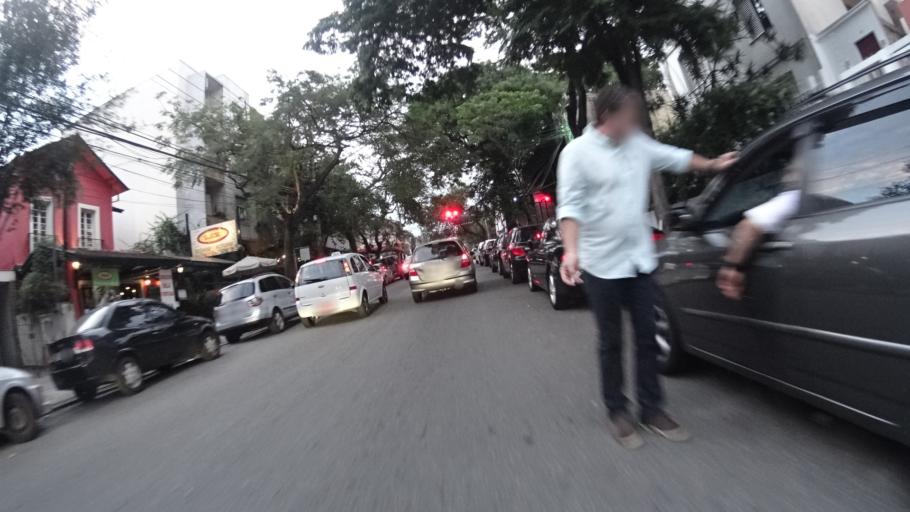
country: BR
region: Sao Paulo
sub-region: Sao Paulo
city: Sao Paulo
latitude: -23.5573
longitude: -46.6919
